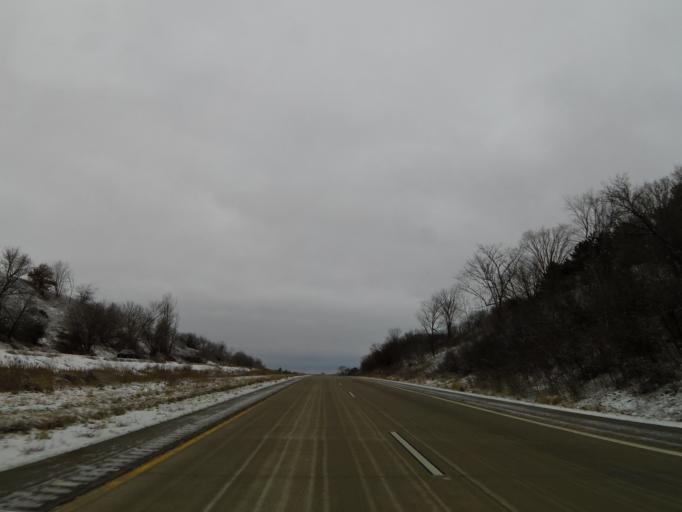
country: US
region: Wisconsin
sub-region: Eau Claire County
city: Eau Claire
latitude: 44.8002
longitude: -91.5541
